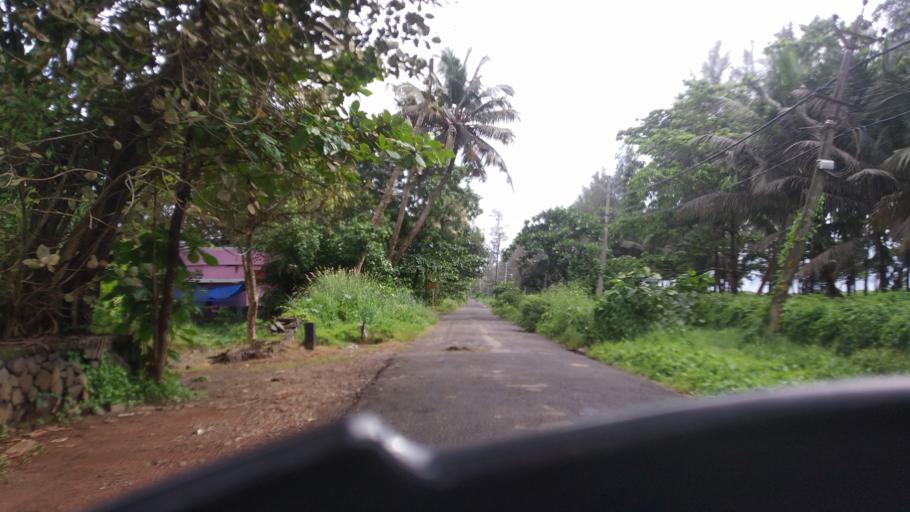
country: IN
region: Kerala
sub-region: Thrissur District
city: Kodungallur
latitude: 10.1229
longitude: 76.1844
